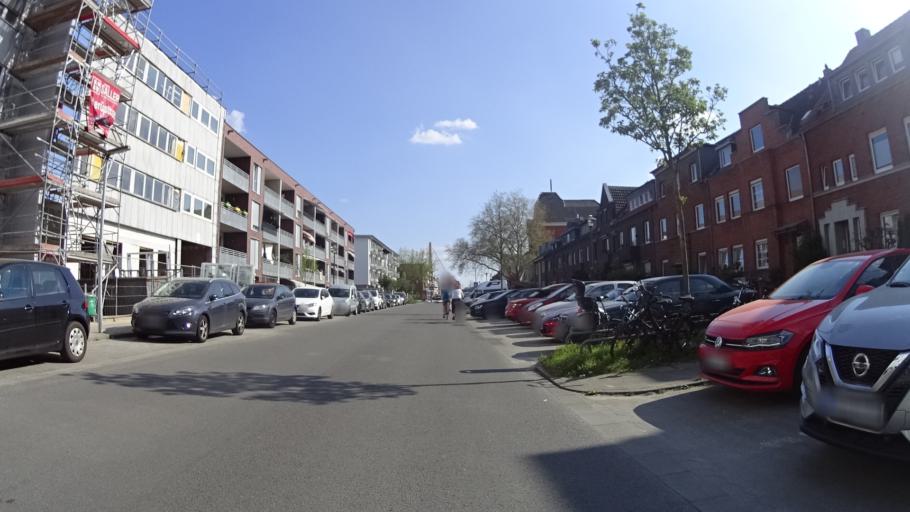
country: DE
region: North Rhine-Westphalia
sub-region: Regierungsbezirk Dusseldorf
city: Dusseldorf
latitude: 51.1949
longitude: 6.7693
